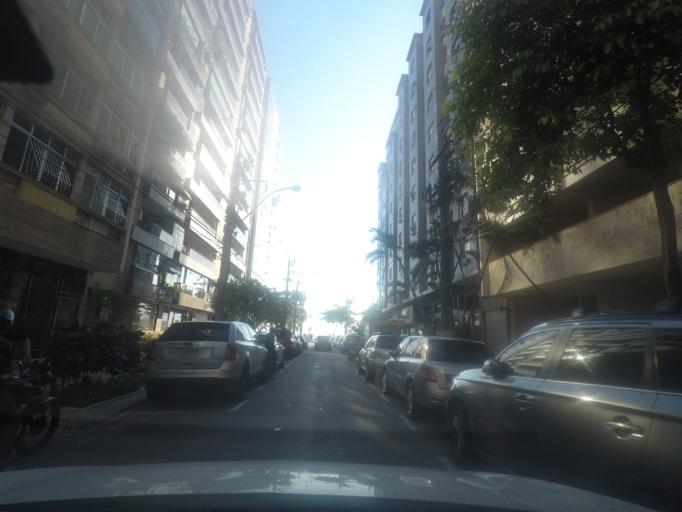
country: BR
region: Rio de Janeiro
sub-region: Niteroi
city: Niteroi
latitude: -22.9048
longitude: -43.1136
